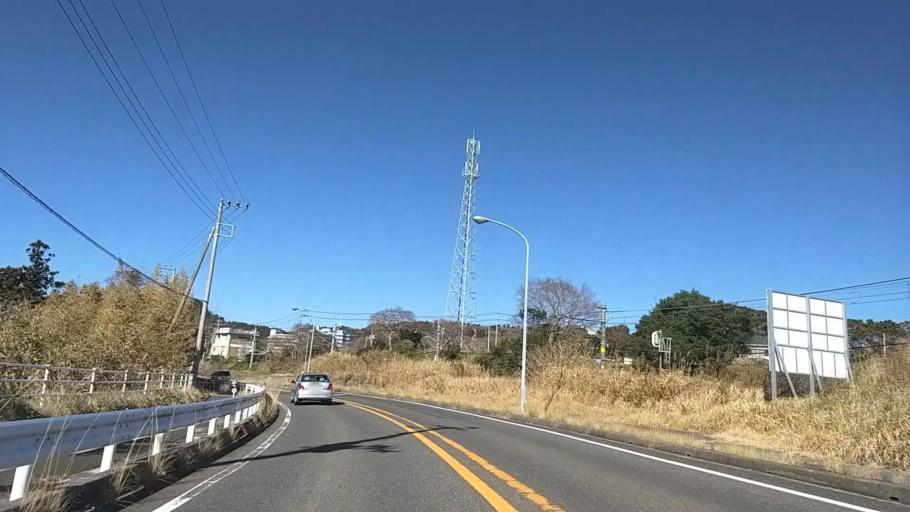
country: JP
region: Chiba
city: Kawaguchi
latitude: 35.0850
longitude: 140.0949
